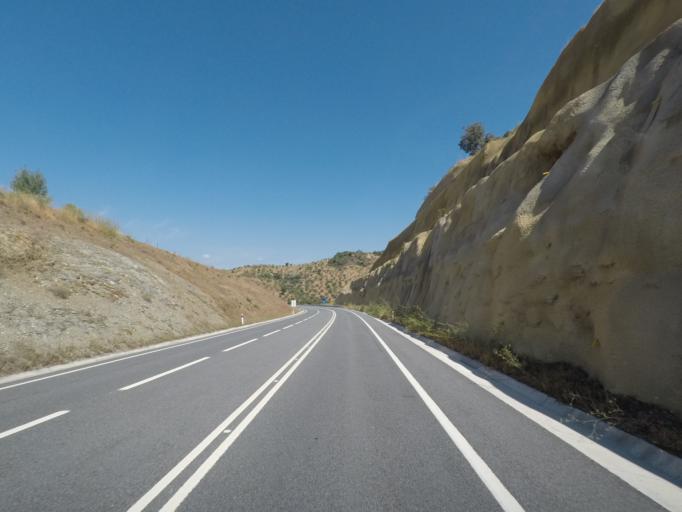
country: PT
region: Braganca
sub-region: Alfandega da Fe
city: Alfandega da Fe
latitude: 41.2929
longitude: -6.8959
